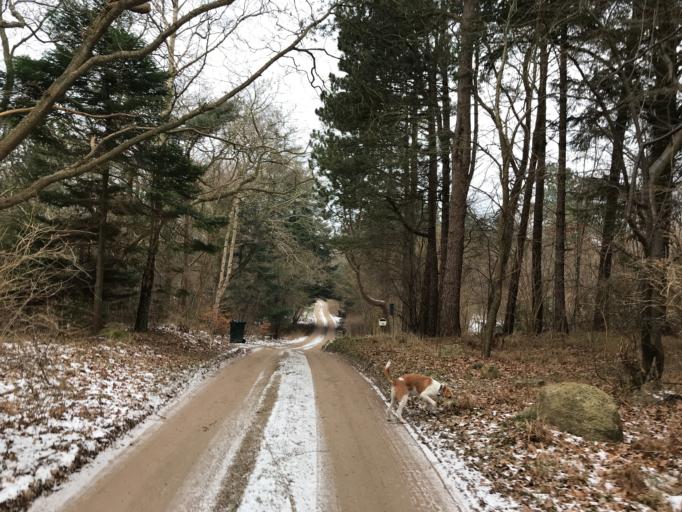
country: DK
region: Zealand
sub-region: Odsherred Kommune
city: Horve
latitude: 55.8186
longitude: 11.3824
